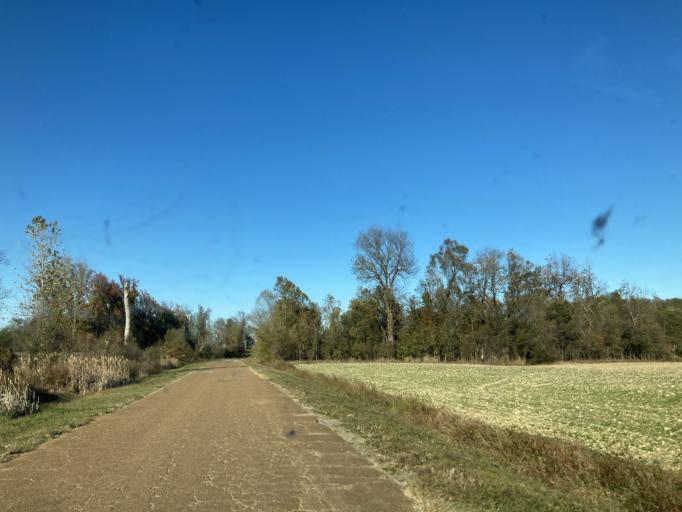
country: US
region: Mississippi
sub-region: Yazoo County
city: Yazoo City
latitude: 32.8125
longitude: -90.4513
